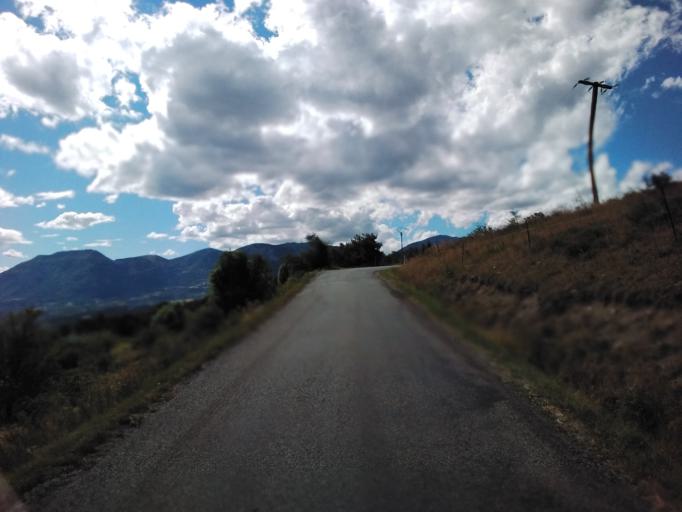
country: FR
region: Provence-Alpes-Cote d'Azur
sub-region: Departement des Hautes-Alpes
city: La Batie-Neuve
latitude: 44.5895
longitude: 6.1486
